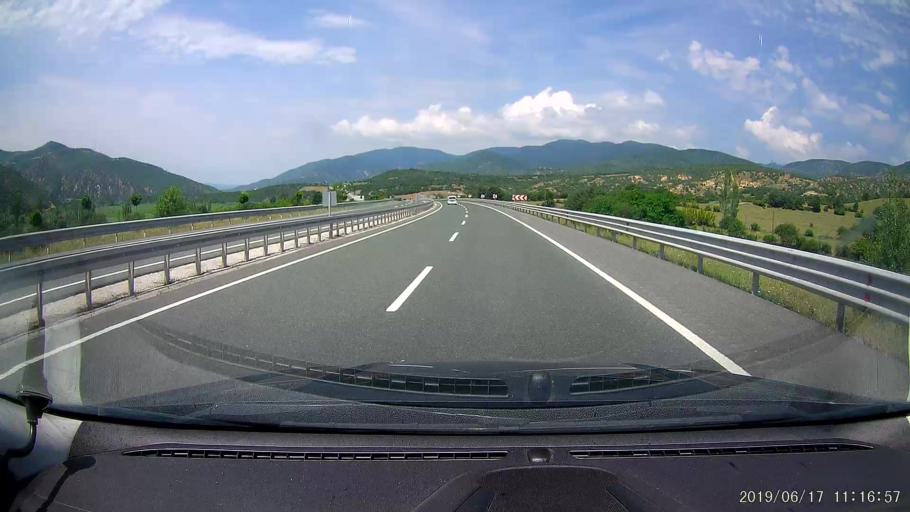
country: TR
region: Kastamonu
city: Tosya
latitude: 40.9433
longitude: 33.8875
